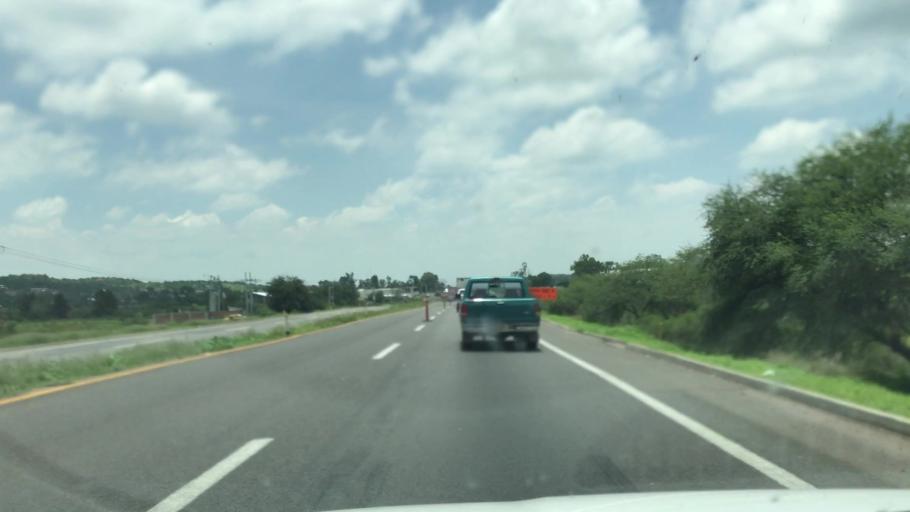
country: MX
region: Guanajuato
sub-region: Irapuato
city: San Ignacio de Rivera (Ojo de Agua)
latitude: 20.5264
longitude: -101.4619
